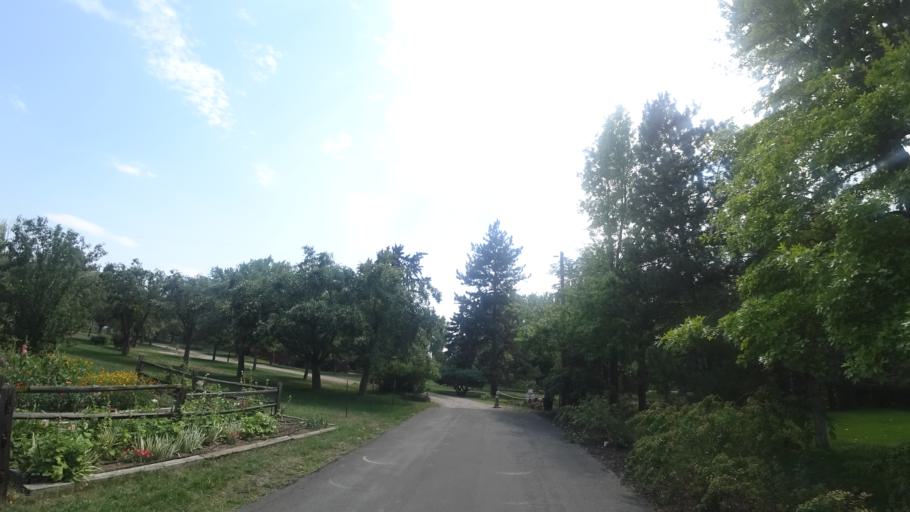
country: US
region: Colorado
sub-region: Arapahoe County
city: Greenwood Village
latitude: 39.6171
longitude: -104.9753
